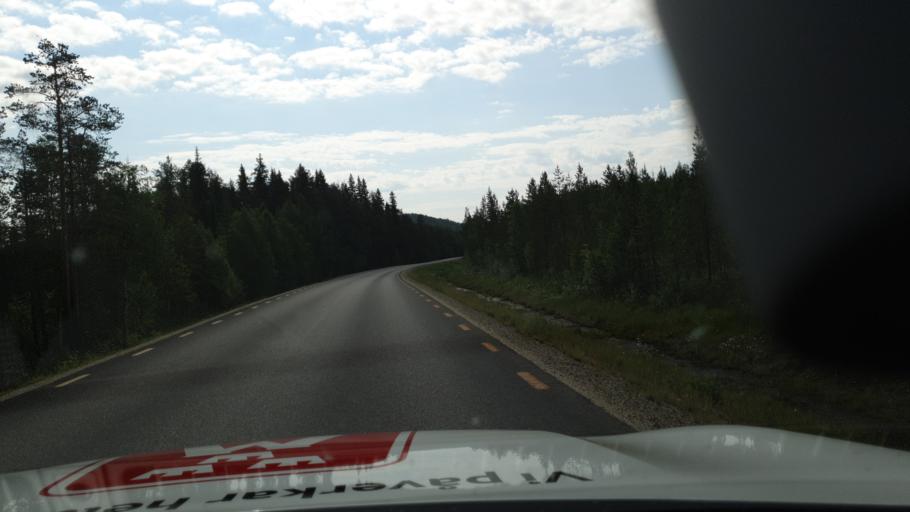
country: SE
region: Vaesterbotten
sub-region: Vindelns Kommun
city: Vindeln
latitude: 64.4625
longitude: 19.3284
